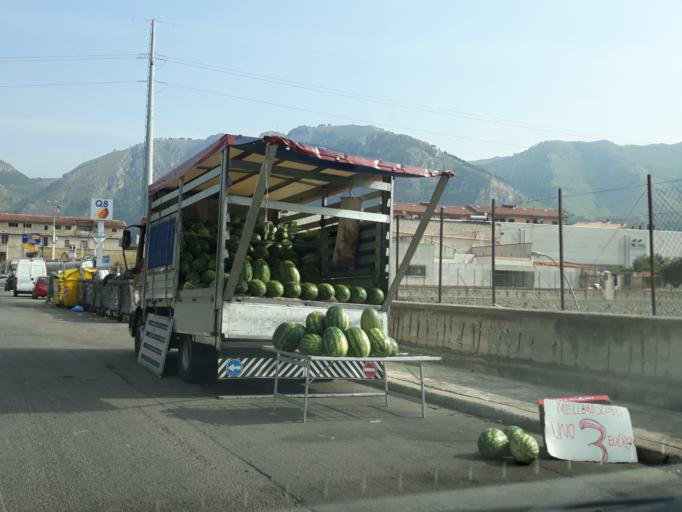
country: IT
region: Sicily
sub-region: Palermo
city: Villa Ciambra
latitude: 38.0886
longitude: 13.3459
